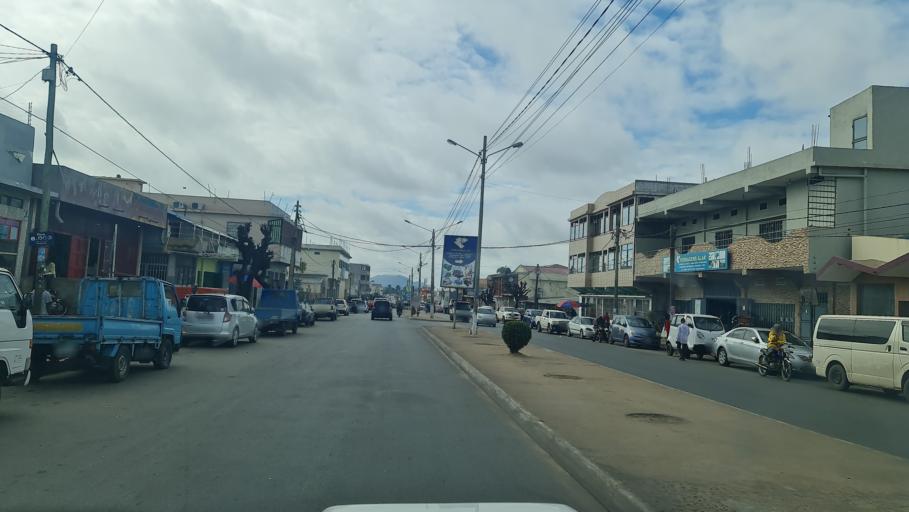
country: MZ
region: Nampula
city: Nampula
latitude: -15.1144
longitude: 39.2737
